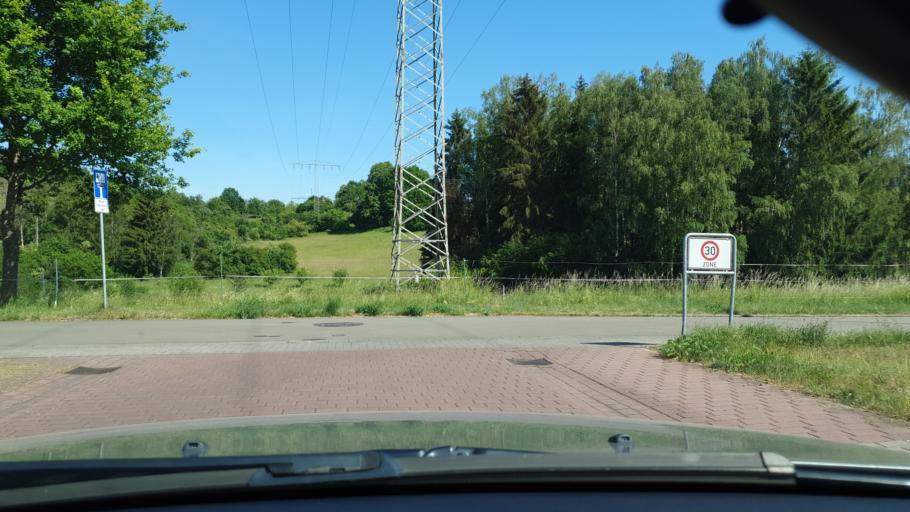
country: DE
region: Rheinland-Pfalz
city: Katzweiler
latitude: 49.4738
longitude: 7.6932
